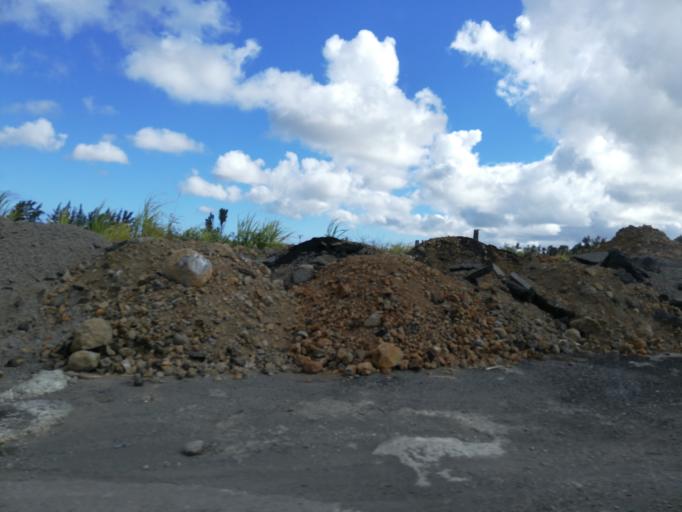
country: MU
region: Grand Port
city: Plaine Magnien
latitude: -20.4281
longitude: 57.6525
